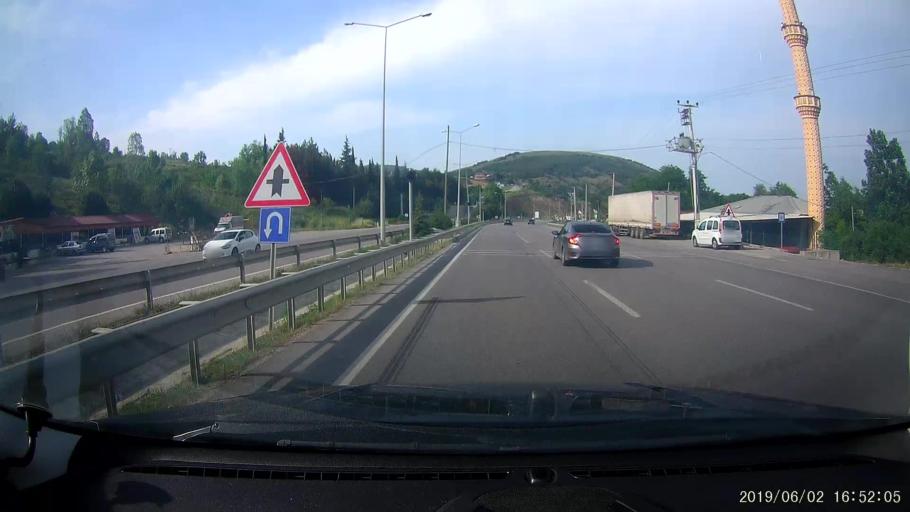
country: TR
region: Samsun
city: Samsun
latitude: 41.2828
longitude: 36.1919
